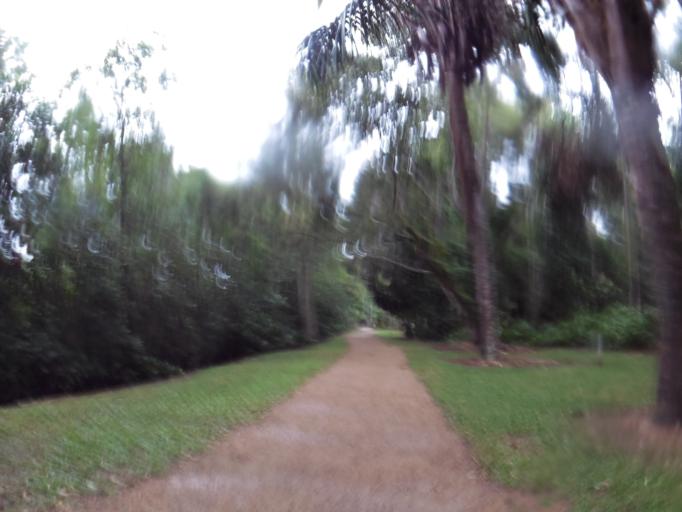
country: AU
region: Queensland
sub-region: Cairns
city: Cairns
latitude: -16.9020
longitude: 145.7507
